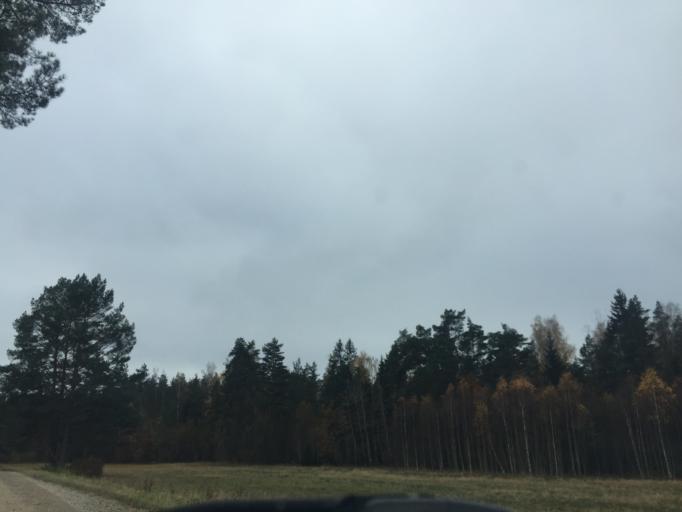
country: LV
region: Jaunpils
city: Jaunpils
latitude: 56.6936
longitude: 23.1163
